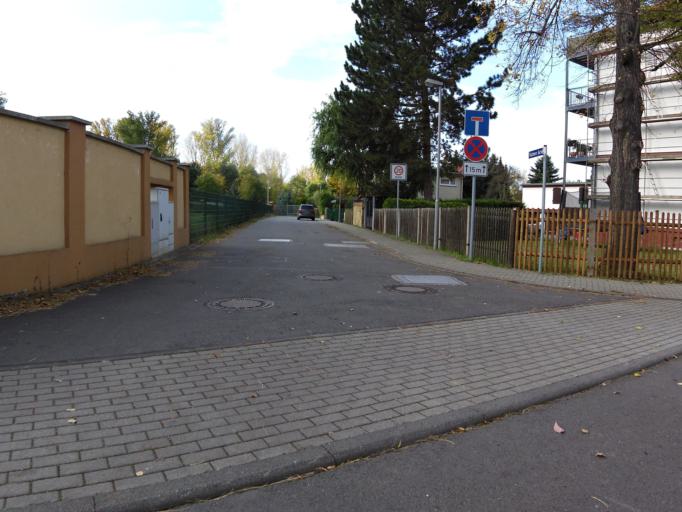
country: DE
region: Saxony
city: Grossposna
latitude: 51.3052
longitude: 12.4527
